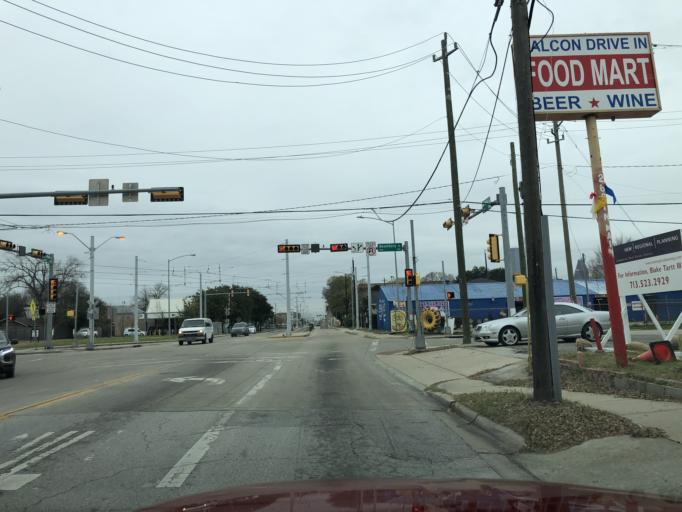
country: US
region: Texas
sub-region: Harris County
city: Houston
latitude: 29.7835
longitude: -95.3652
